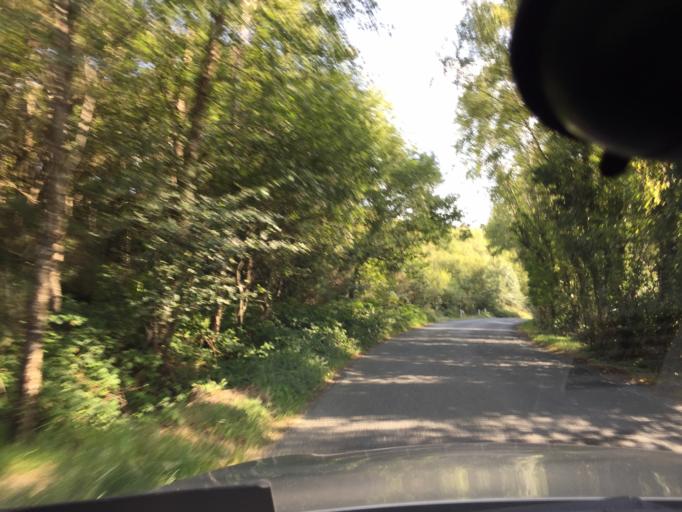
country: IE
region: Leinster
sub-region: Wicklow
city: Rathdrum
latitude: 53.0109
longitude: -6.2958
